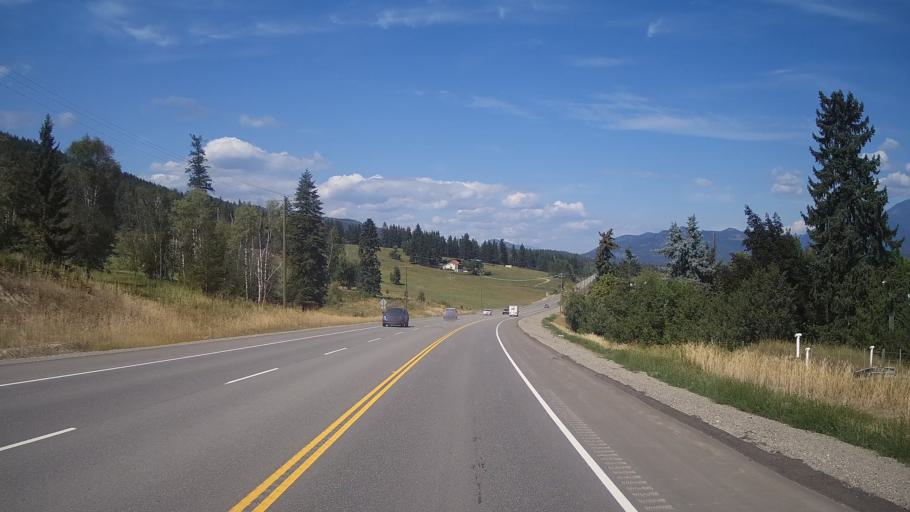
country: CA
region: British Columbia
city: Kamloops
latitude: 51.2982
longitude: -120.1817
